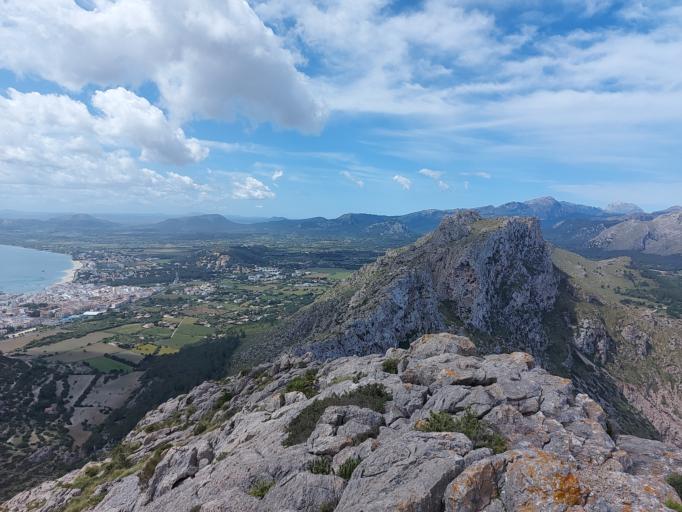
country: ES
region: Balearic Islands
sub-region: Illes Balears
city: Pollenca
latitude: 39.9249
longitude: 3.0823
